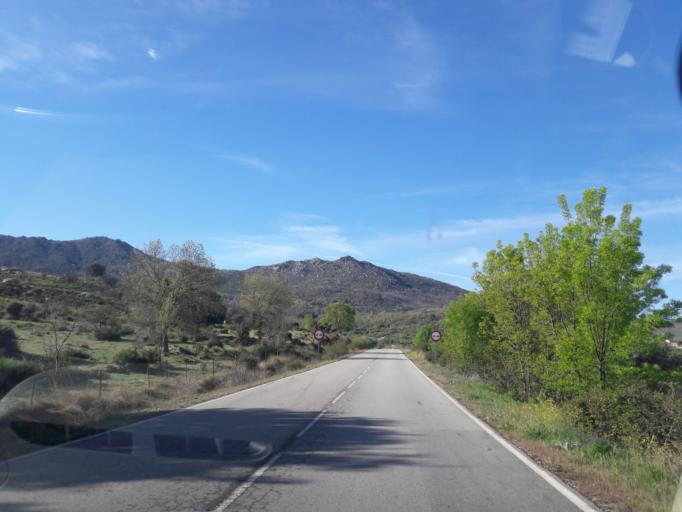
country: ES
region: Castille and Leon
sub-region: Provincia de Salamanca
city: Sanchotello
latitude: 40.4509
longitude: -5.7359
